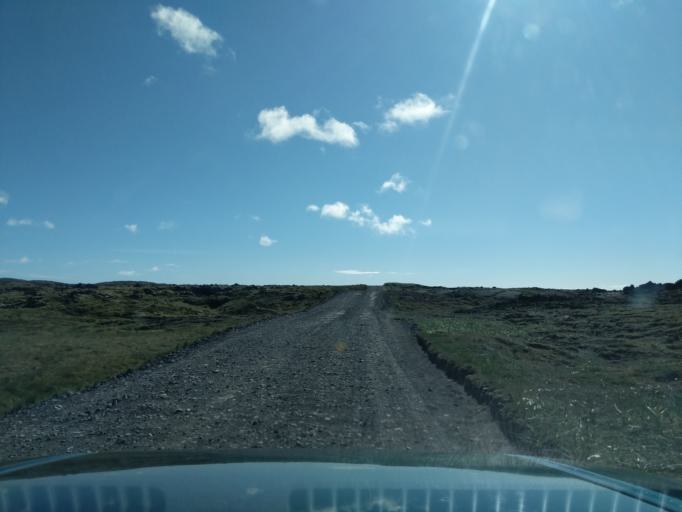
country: IS
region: West
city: Olafsvik
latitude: 64.8779
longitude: -23.9927
